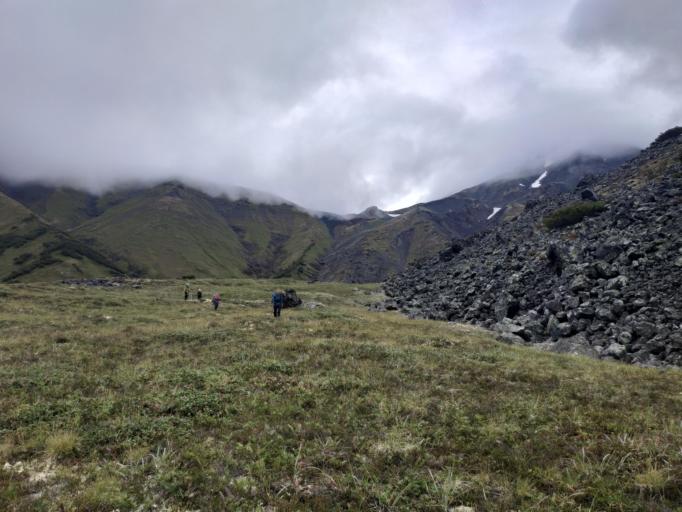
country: RU
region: Kamtsjatka
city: Yelizovo
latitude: 53.8945
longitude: 158.0320
